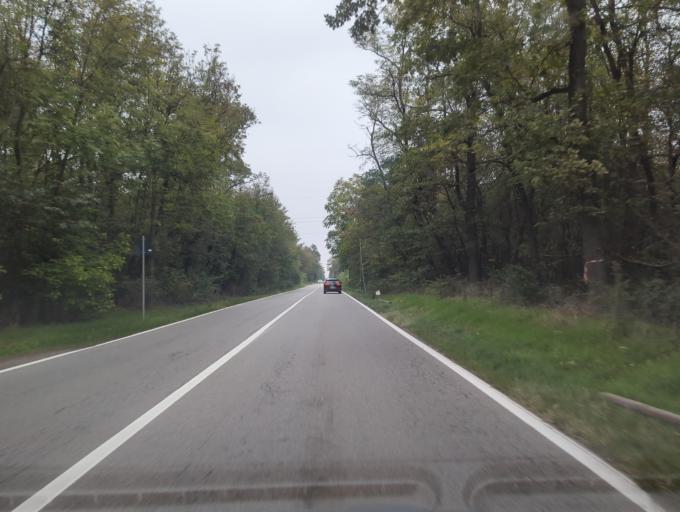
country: IT
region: Piedmont
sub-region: Provincia di Novara
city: Galliate
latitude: 45.4962
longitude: 8.7192
